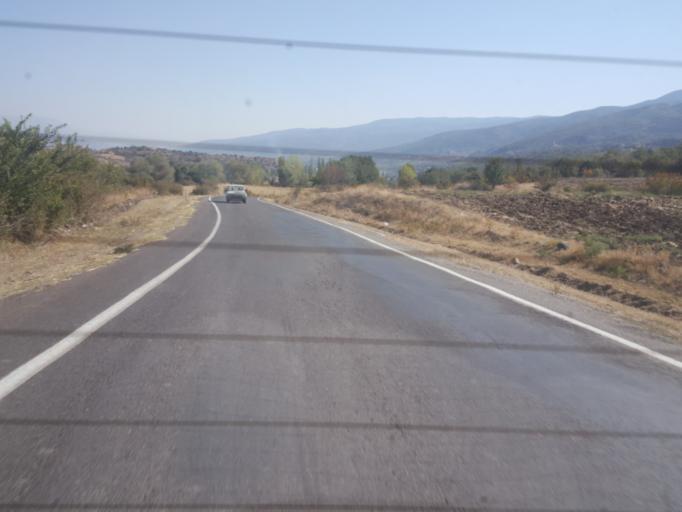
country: TR
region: Kastamonu
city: Tosya
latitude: 40.9861
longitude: 34.0836
